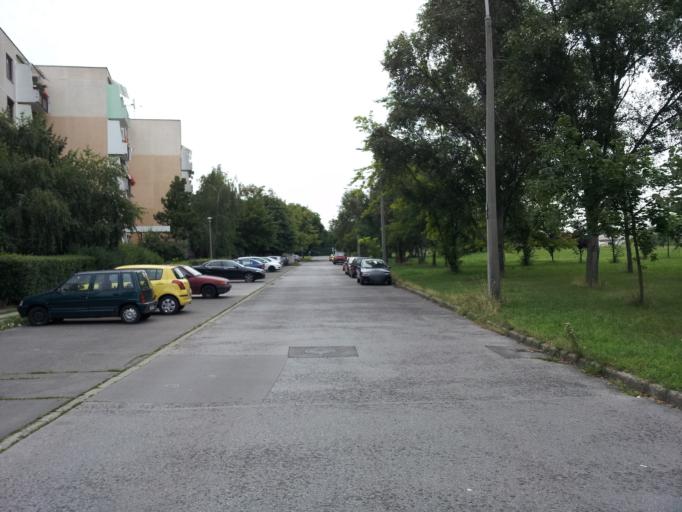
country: HU
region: Budapest
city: Budapest XXI. keruelet
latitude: 47.4061
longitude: 19.0586
